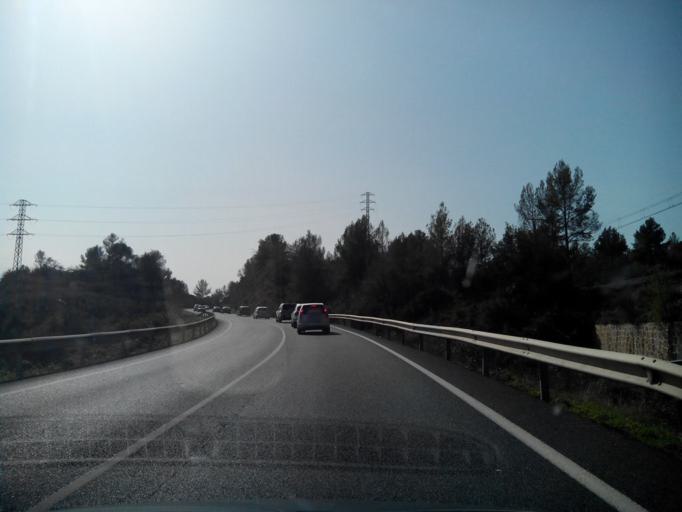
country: ES
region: Catalonia
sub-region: Provincia de Tarragona
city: Alcover
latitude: 41.2901
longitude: 1.1880
